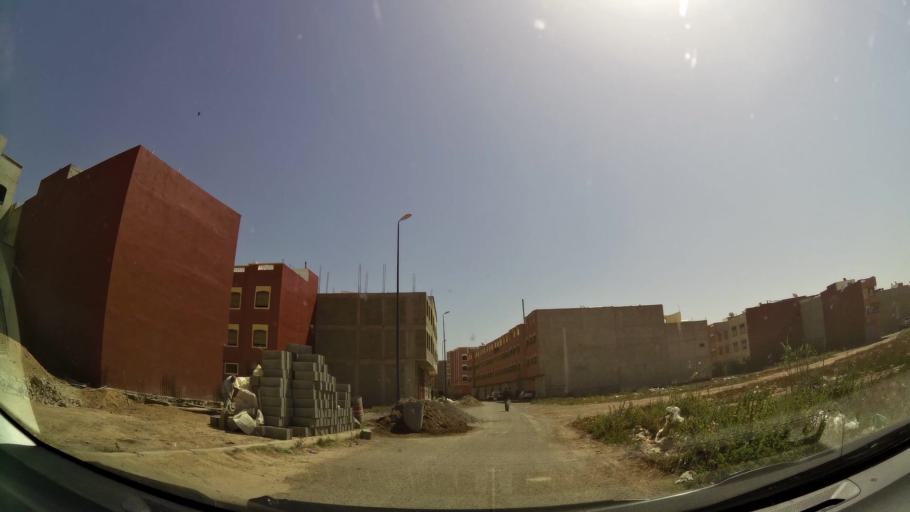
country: MA
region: Souss-Massa-Draa
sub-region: Inezgane-Ait Mellou
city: Inezgane
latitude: 30.3378
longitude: -9.5094
